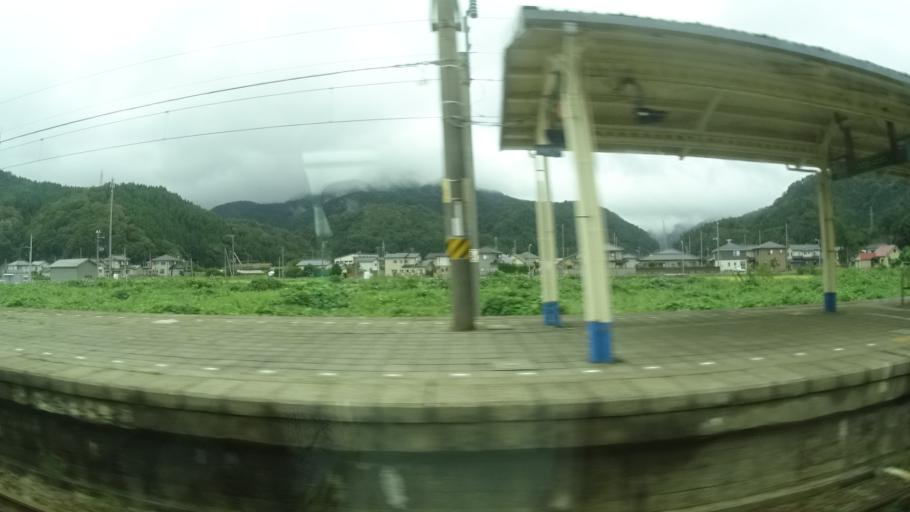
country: JP
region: Yamagata
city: Tsuruoka
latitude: 38.5553
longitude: 139.5487
